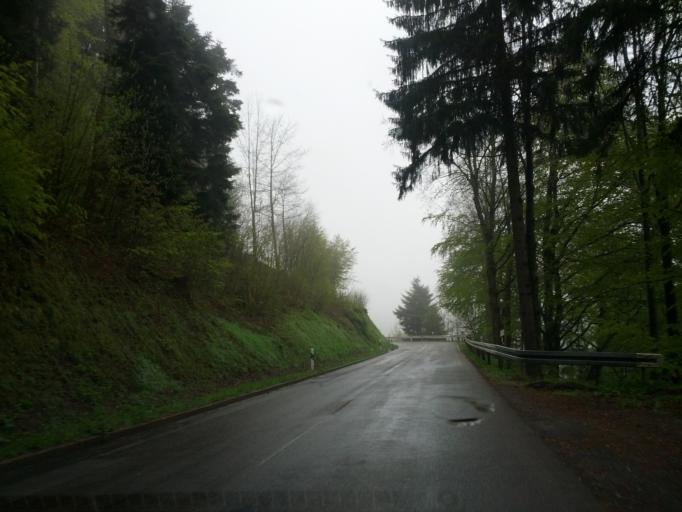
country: DE
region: Baden-Wuerttemberg
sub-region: Freiburg Region
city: Wieden
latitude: 47.8694
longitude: 7.8519
